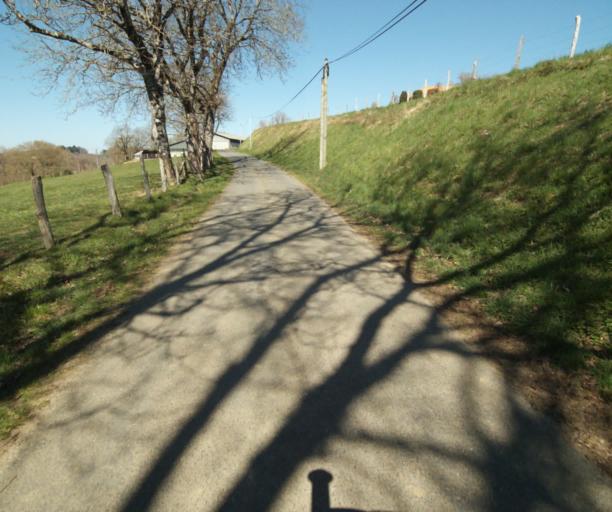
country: FR
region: Limousin
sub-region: Departement de la Correze
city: Saint-Clement
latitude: 45.3225
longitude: 1.7100
